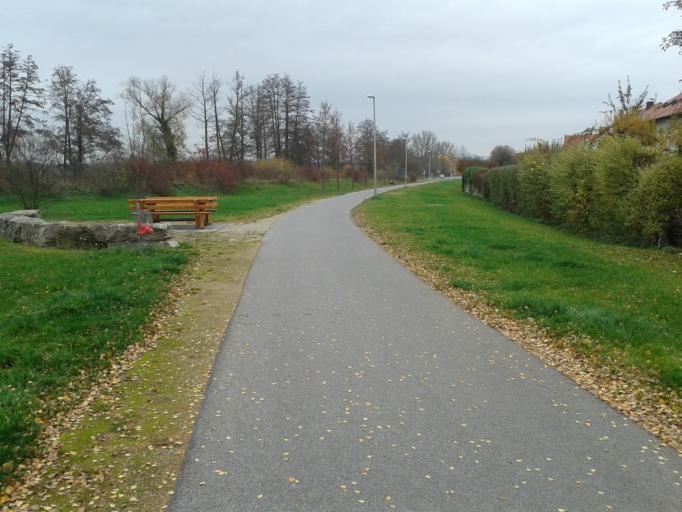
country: DE
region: Bavaria
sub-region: Upper Franconia
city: Memmelsdorf
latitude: 49.9359
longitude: 10.9596
